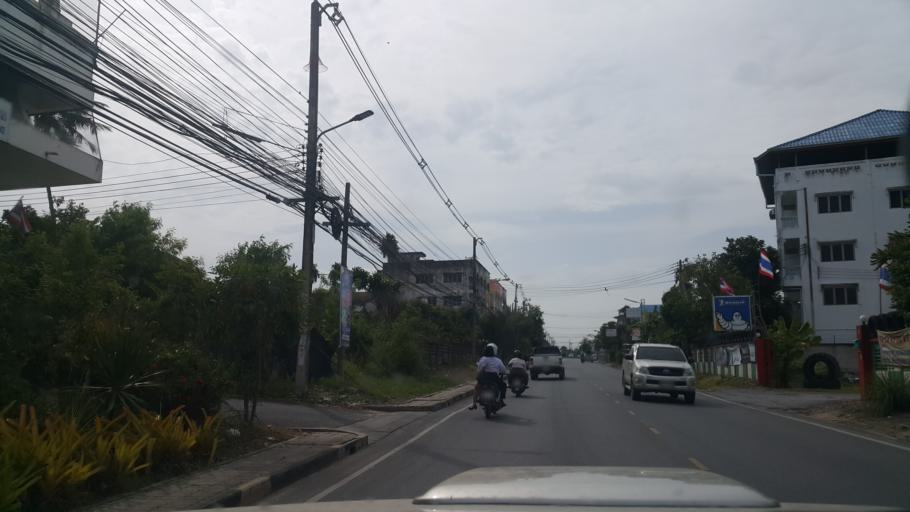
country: TH
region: Rayong
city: Ban Chang
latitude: 12.7304
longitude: 101.0504
